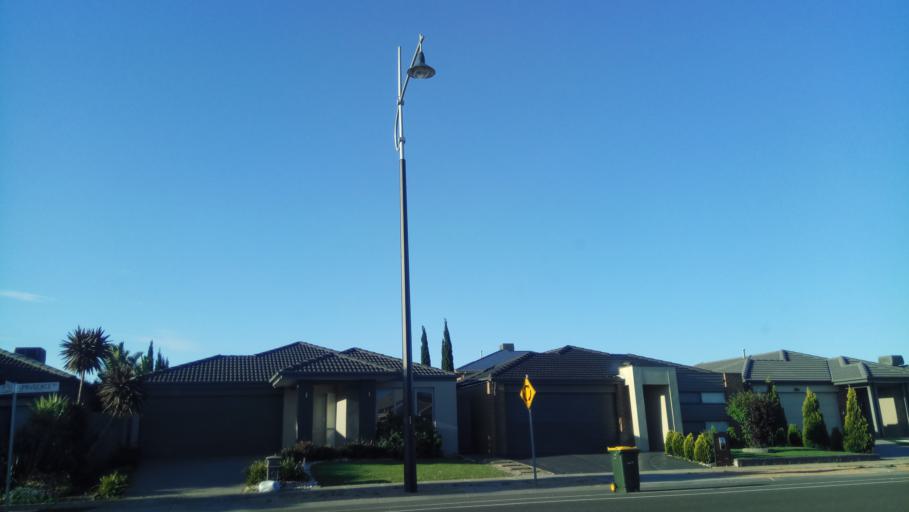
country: AU
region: Victoria
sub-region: Wyndham
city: Point Cook
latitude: -37.9070
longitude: 144.7364
